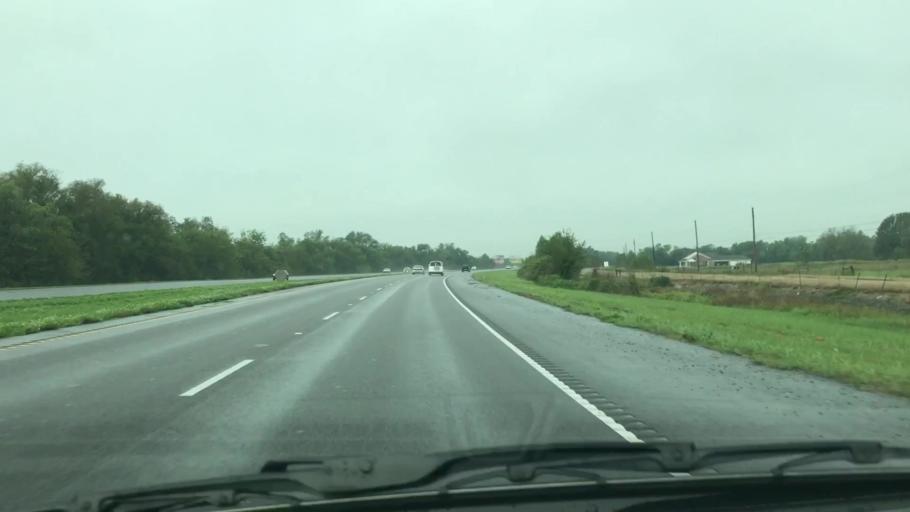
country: US
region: Louisiana
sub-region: Lafourche Parish
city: Raceland
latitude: 29.6911
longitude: -90.5916
